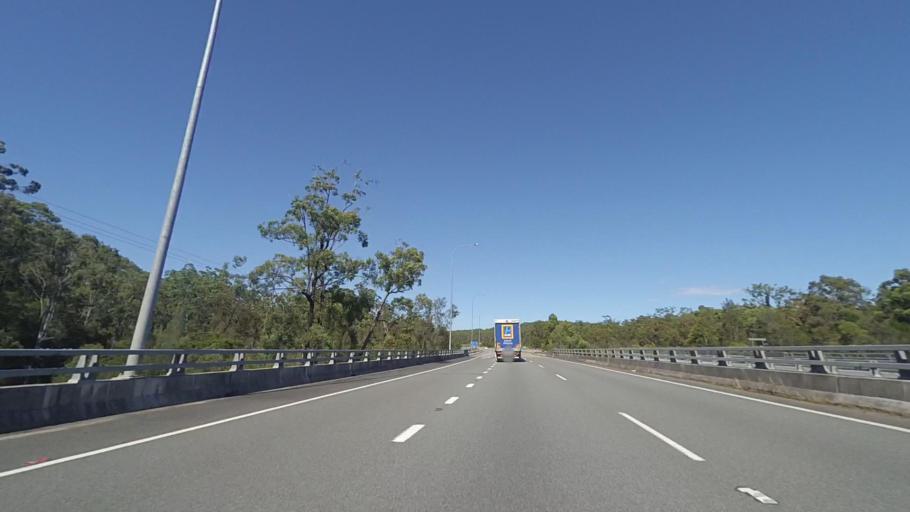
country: AU
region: New South Wales
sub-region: Port Stephens Shire
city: Port Stephens
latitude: -32.6114
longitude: 152.0856
